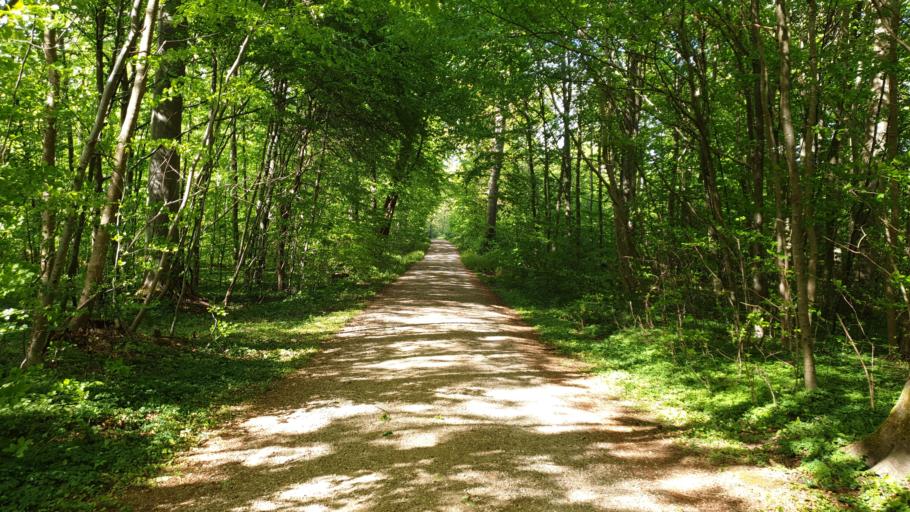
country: DK
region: South Denmark
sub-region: Sonderborg Kommune
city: Grasten
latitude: 54.9227
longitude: 9.5857
